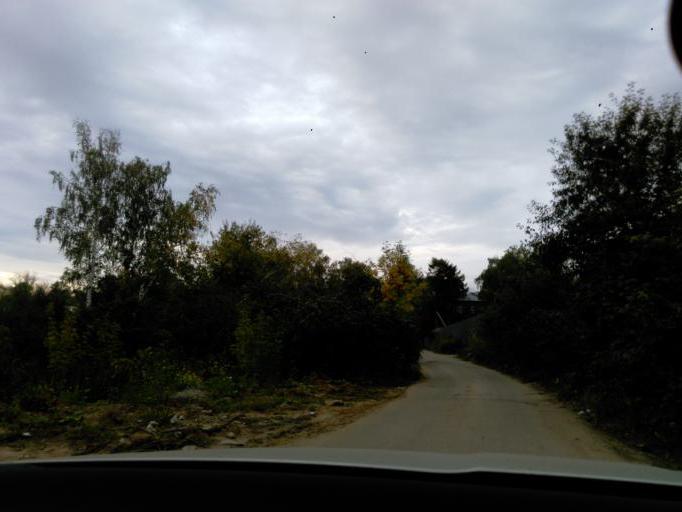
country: RU
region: Moscow
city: Severnyy
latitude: 55.9437
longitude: 37.5340
